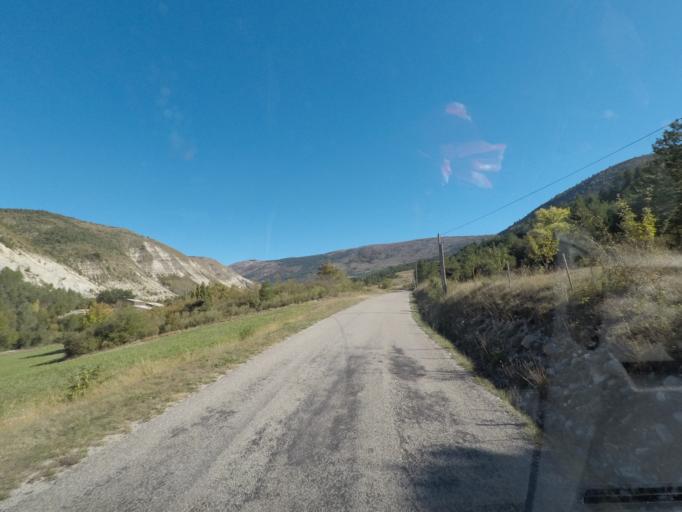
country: FR
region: Rhone-Alpes
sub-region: Departement de la Drome
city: Die
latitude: 44.5199
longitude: 5.3490
